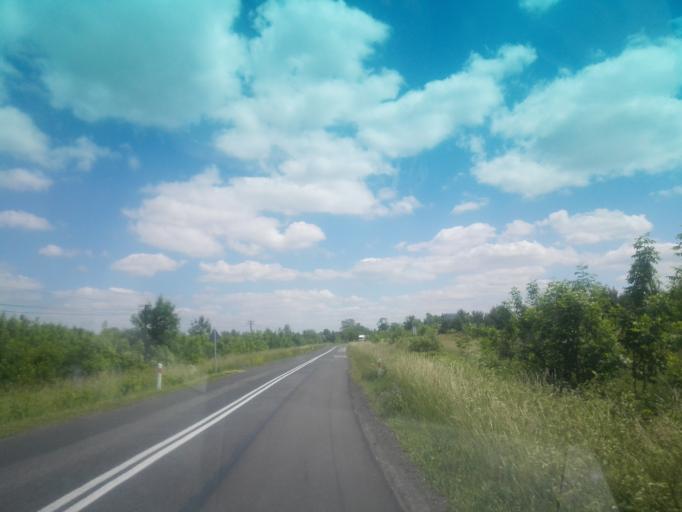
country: PL
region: Silesian Voivodeship
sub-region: Powiat czestochowski
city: Potok Zloty
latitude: 50.7363
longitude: 19.3892
